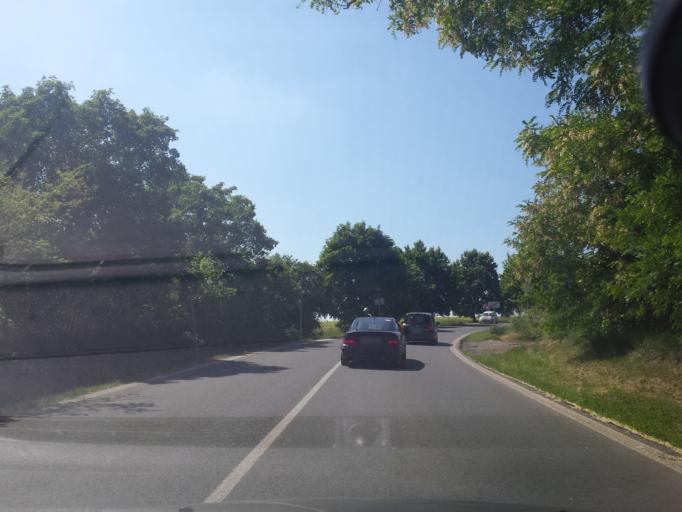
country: CZ
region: Central Bohemia
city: Horomerice
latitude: 50.1169
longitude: 14.3621
